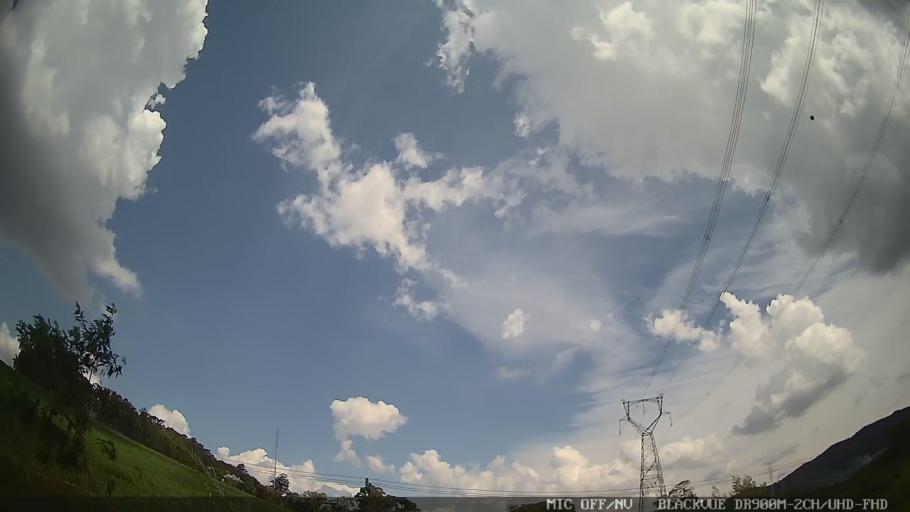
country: BR
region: Sao Paulo
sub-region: Braganca Paulista
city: Braganca Paulista
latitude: -22.9517
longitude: -46.6000
